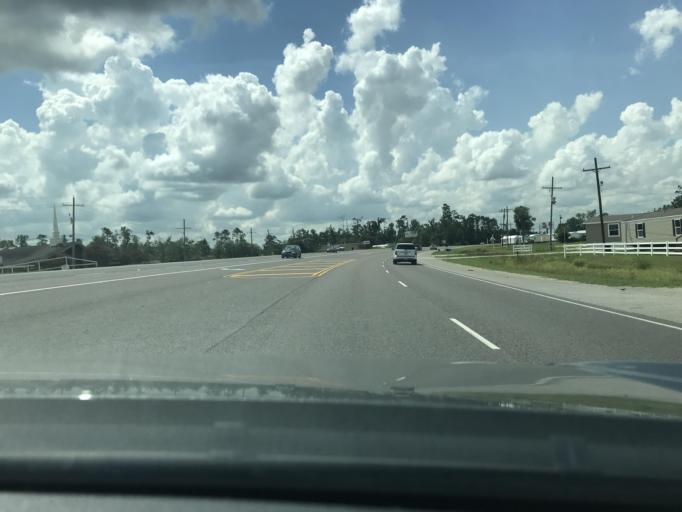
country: US
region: Louisiana
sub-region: Calcasieu Parish
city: Moss Bluff
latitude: 30.3111
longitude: -93.1955
